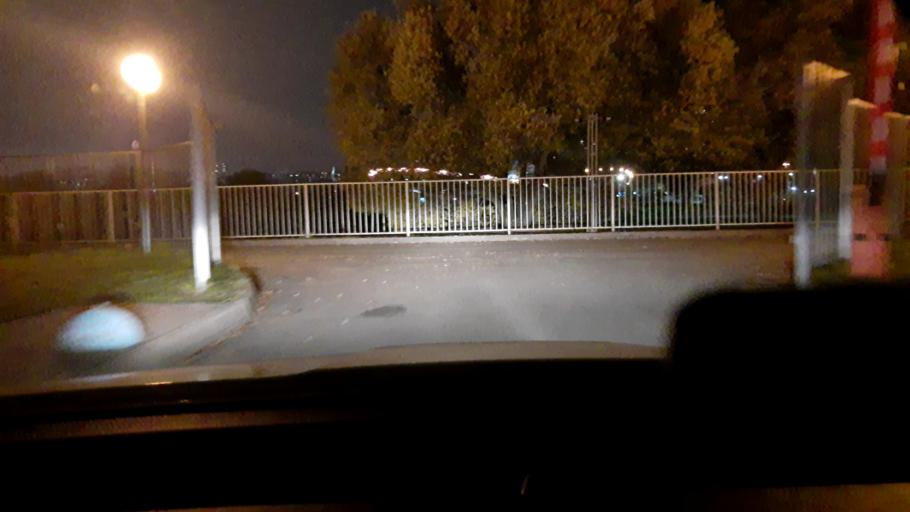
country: RU
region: Moscow
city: Shchukino
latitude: 55.7656
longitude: 37.4380
